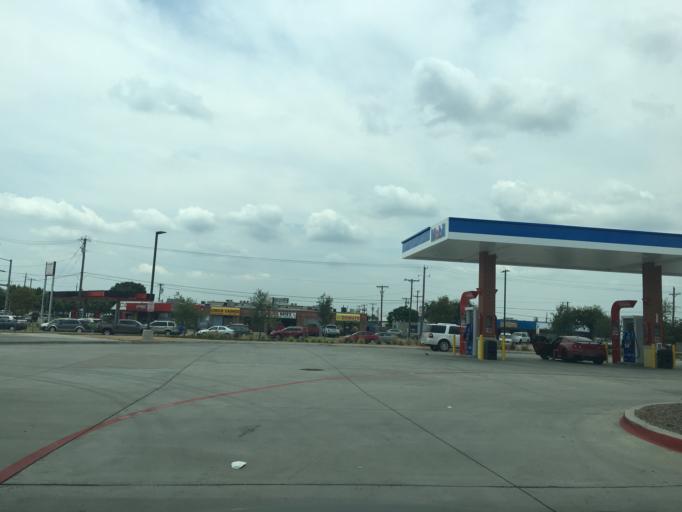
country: US
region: Texas
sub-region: Dallas County
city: Garland
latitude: 32.8950
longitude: -96.6823
